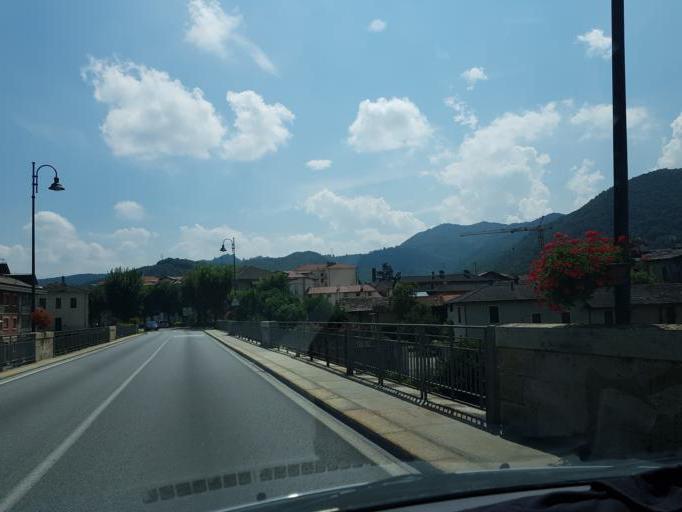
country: IT
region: Piedmont
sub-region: Provincia di Cuneo
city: Dronero
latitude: 44.4648
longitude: 7.3662
